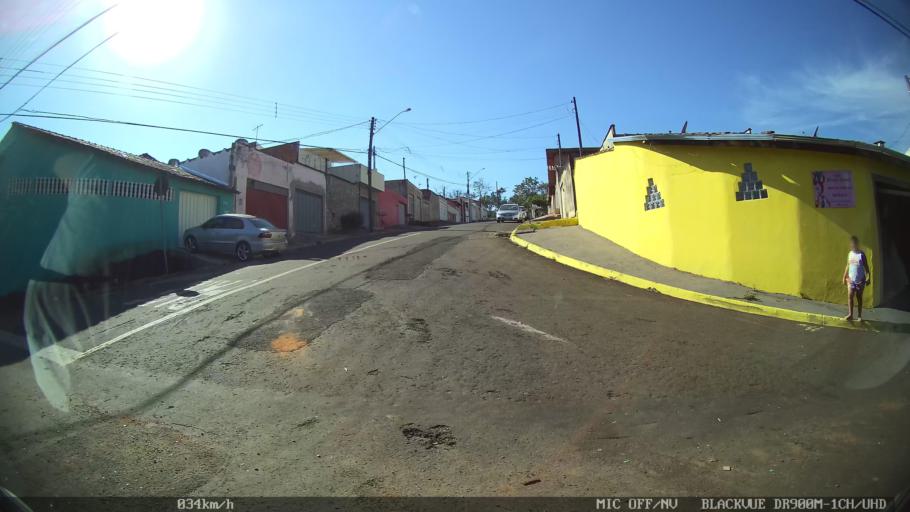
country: BR
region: Sao Paulo
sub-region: Franca
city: Franca
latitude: -20.4915
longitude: -47.4179
